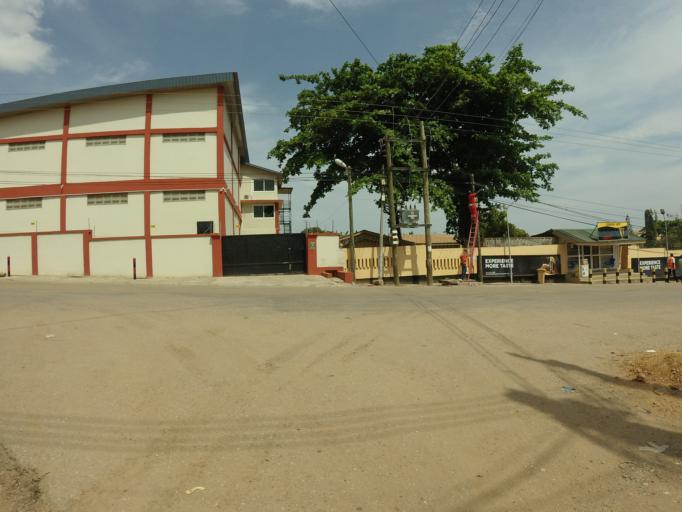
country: GH
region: Greater Accra
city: Dome
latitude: 5.6304
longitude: -0.2354
